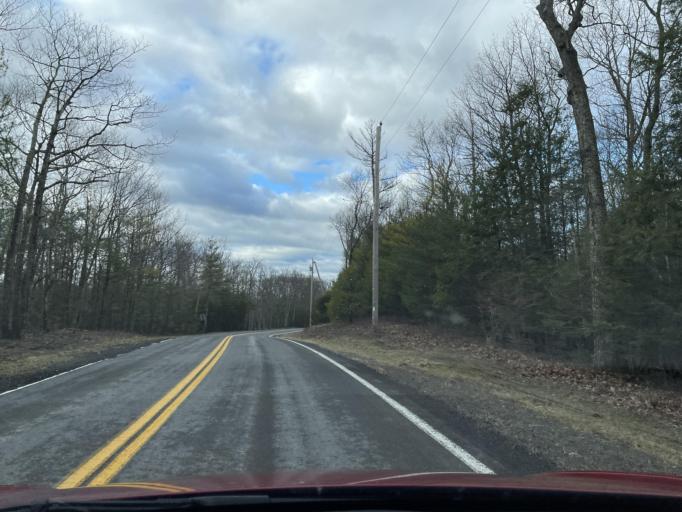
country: US
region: New York
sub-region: Ulster County
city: Zena
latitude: 42.0648
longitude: -74.0759
